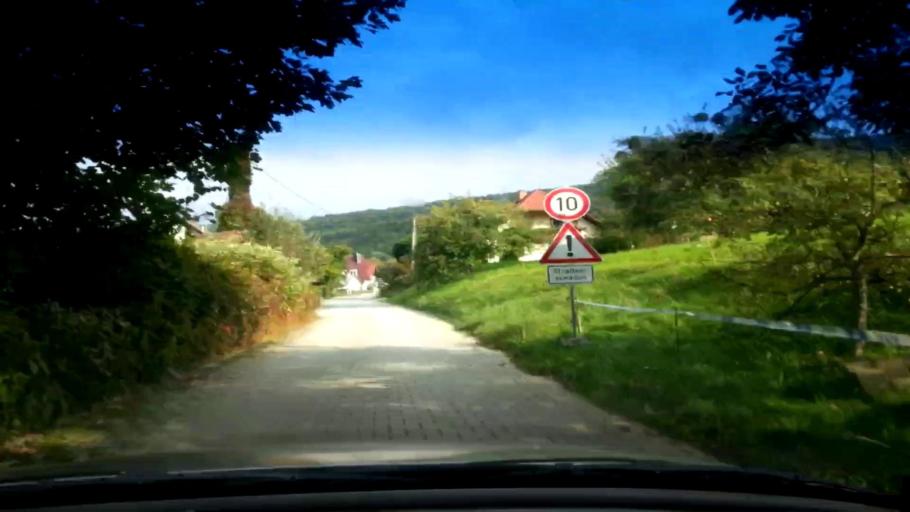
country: DE
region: Bavaria
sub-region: Upper Franconia
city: Schesslitz
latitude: 49.9962
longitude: 11.0755
